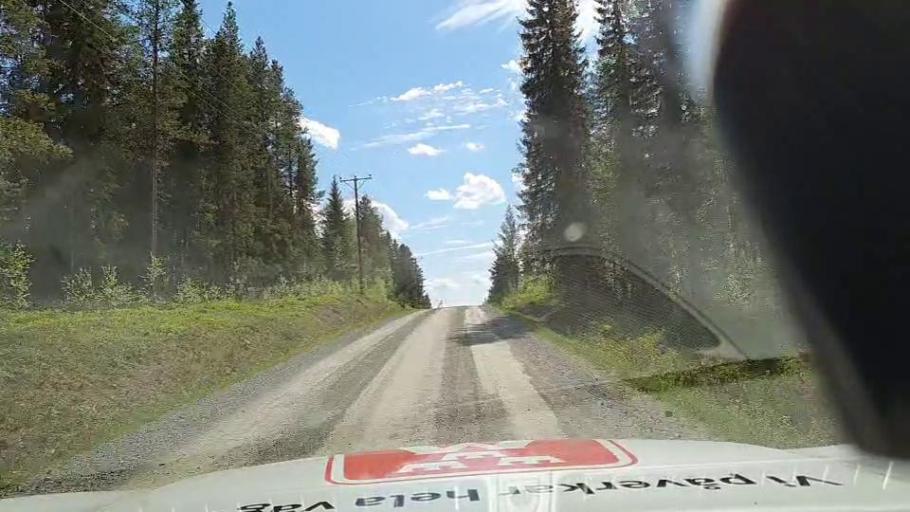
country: SE
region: Jaemtland
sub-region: Stroemsunds Kommun
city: Stroemsund
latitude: 64.4653
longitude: 15.5945
